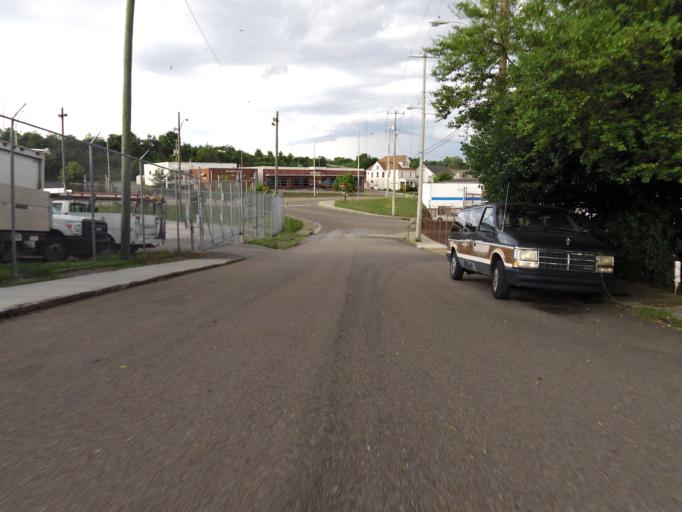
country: US
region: Tennessee
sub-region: Knox County
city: Knoxville
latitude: 35.9766
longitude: -83.9159
